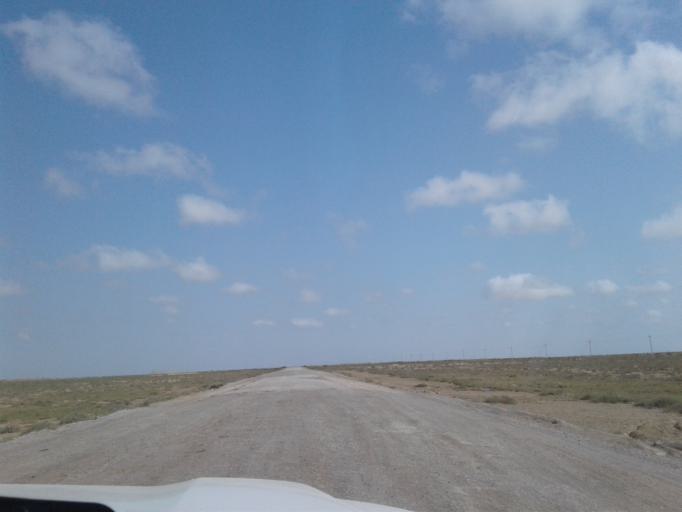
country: IR
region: Golestan
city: Gomishan
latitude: 37.6520
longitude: 53.9320
